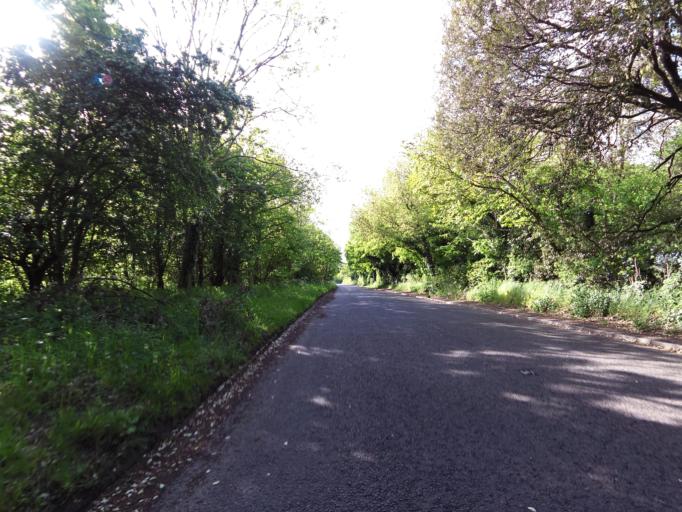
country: GB
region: England
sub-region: Suffolk
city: Beccles
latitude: 52.4506
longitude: 1.6083
